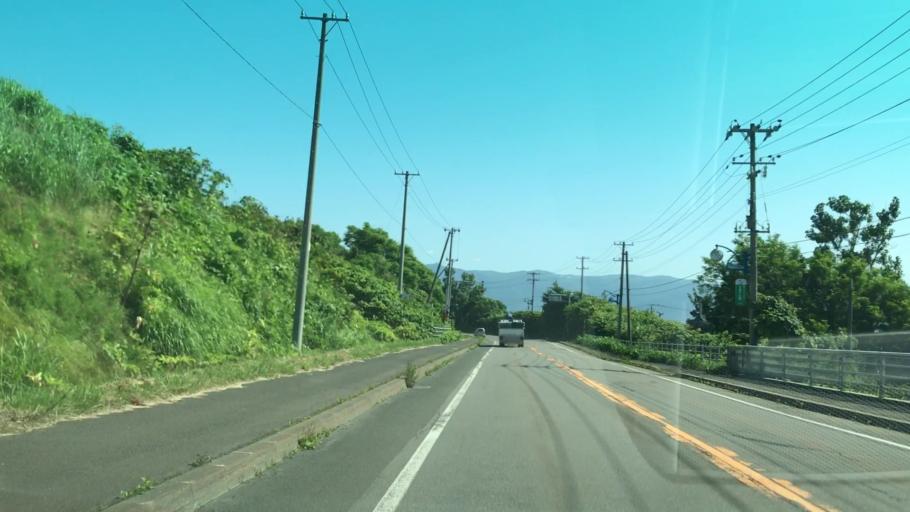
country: JP
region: Hokkaido
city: Iwanai
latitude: 43.0612
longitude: 140.4973
